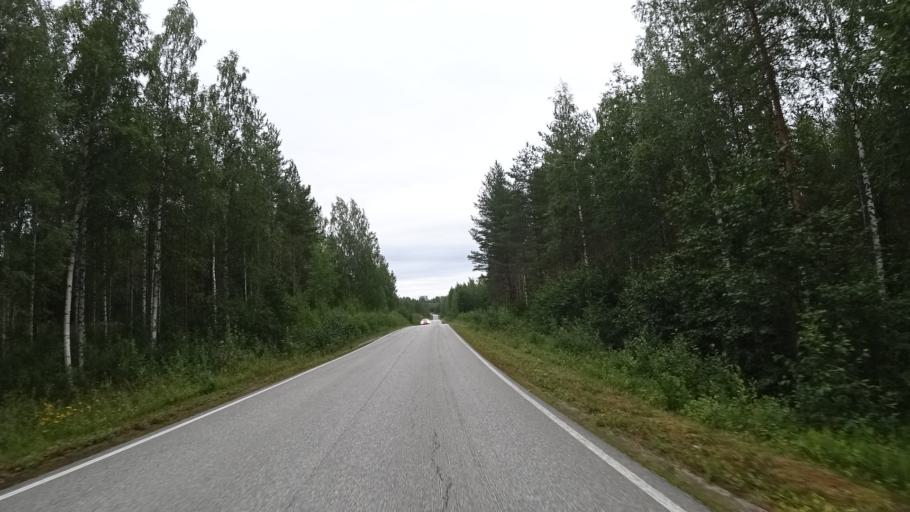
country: FI
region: North Karelia
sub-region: Pielisen Karjala
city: Lieksa
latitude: 63.3688
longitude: 30.2931
